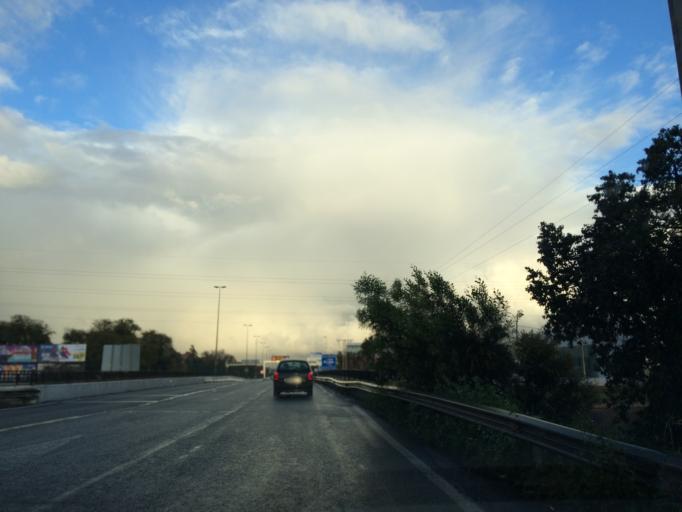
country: ES
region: Andalusia
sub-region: Provincia de Sevilla
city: Sevilla
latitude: 37.3861
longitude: -5.9351
